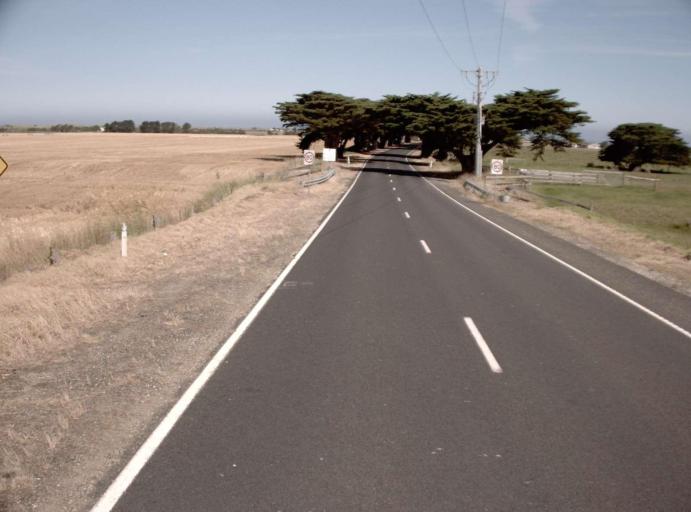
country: AU
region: Victoria
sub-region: Wellington
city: Sale
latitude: -38.3628
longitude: 147.1825
